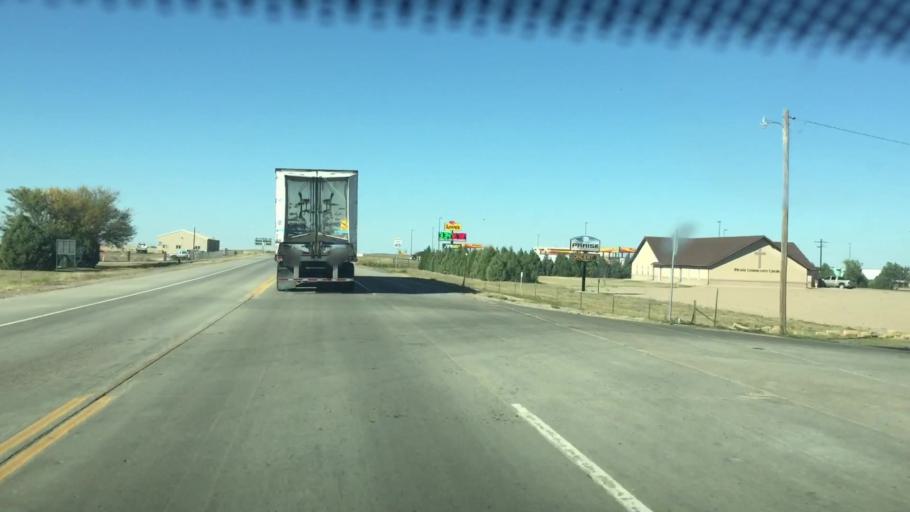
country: US
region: Colorado
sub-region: Kiowa County
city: Eads
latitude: 38.4859
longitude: -102.7857
